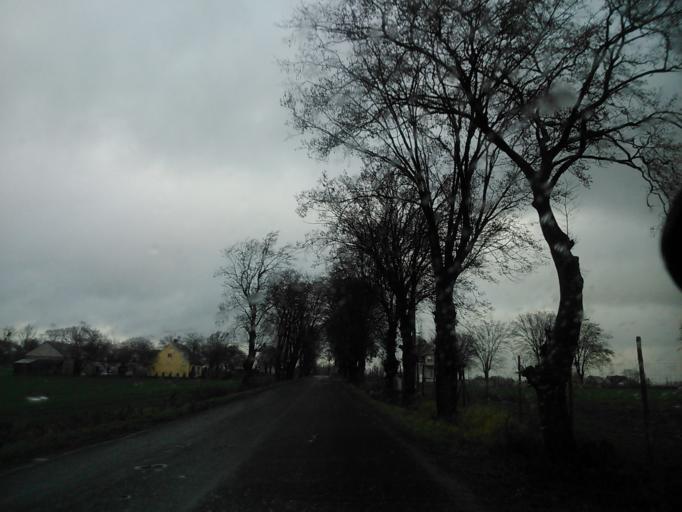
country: PL
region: Kujawsko-Pomorskie
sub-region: Powiat golubsko-dobrzynski
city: Radomin
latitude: 53.1205
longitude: 19.1647
